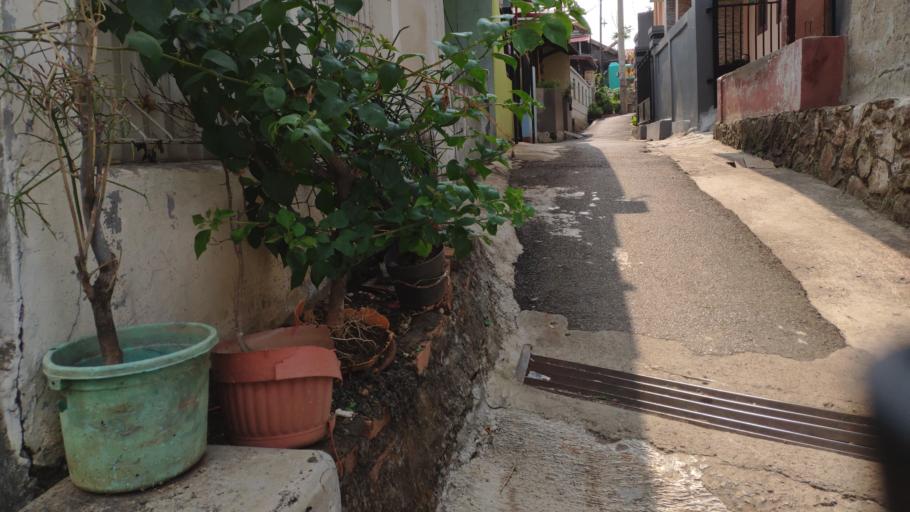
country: ID
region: West Java
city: Depok
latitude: -6.3198
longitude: 106.8162
